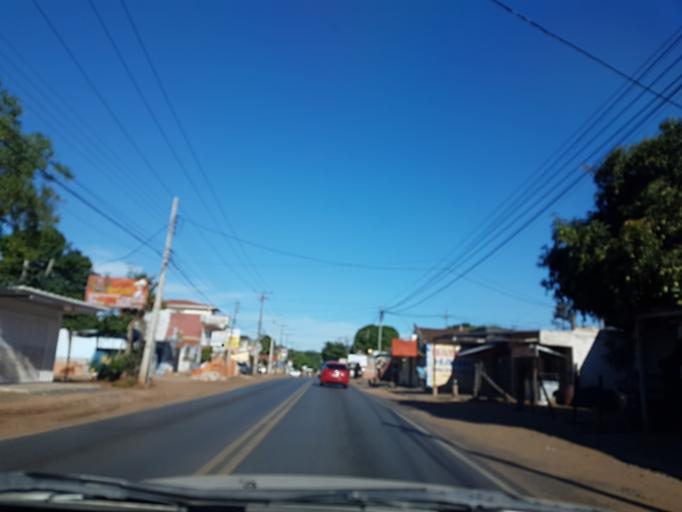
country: PY
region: Central
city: San Lorenzo
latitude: -25.2743
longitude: -57.4816
